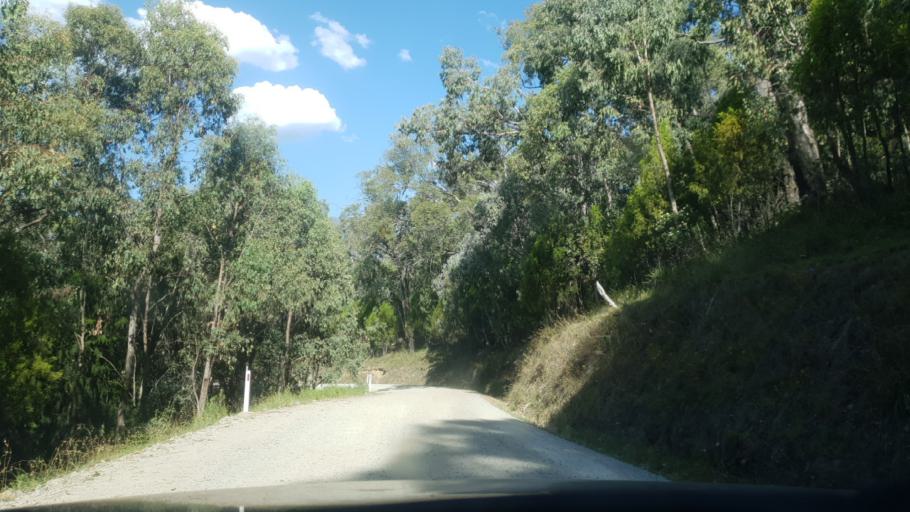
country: AU
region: Victoria
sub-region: Alpine
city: Mount Beauty
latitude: -36.7474
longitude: 147.1835
